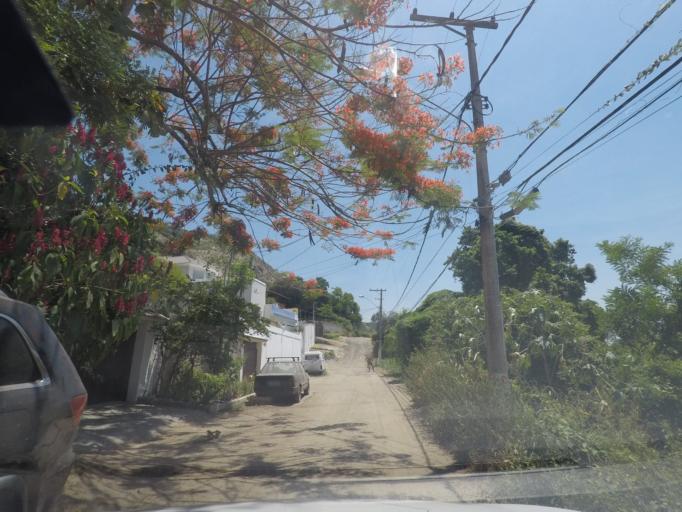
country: BR
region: Rio de Janeiro
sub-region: Niteroi
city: Niteroi
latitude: -22.9713
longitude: -43.0437
